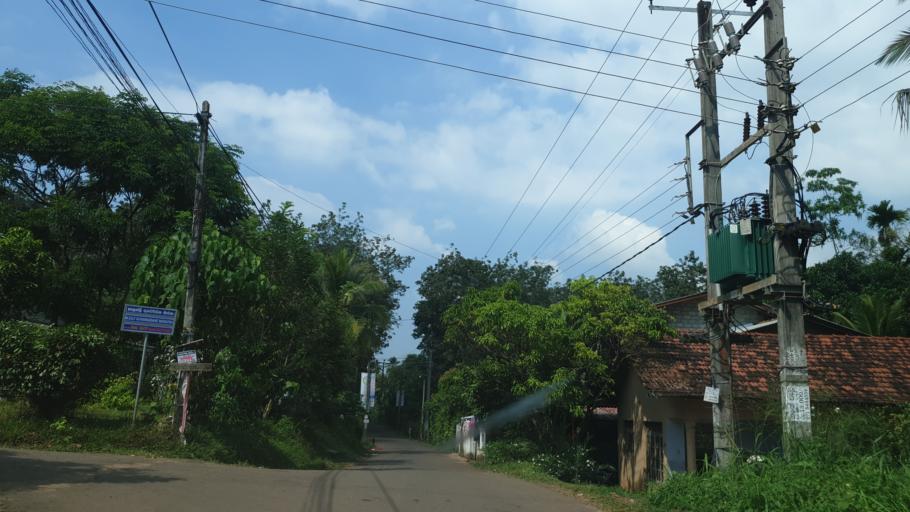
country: LK
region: Western
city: Panadura
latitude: 6.7281
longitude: 79.9537
